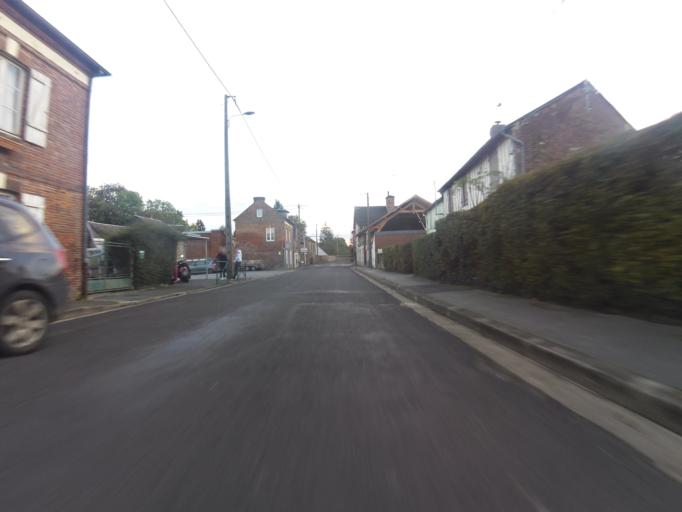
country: FR
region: Lower Normandy
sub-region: Departement de l'Orne
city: Vimoutiers
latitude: 48.9289
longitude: 0.2660
